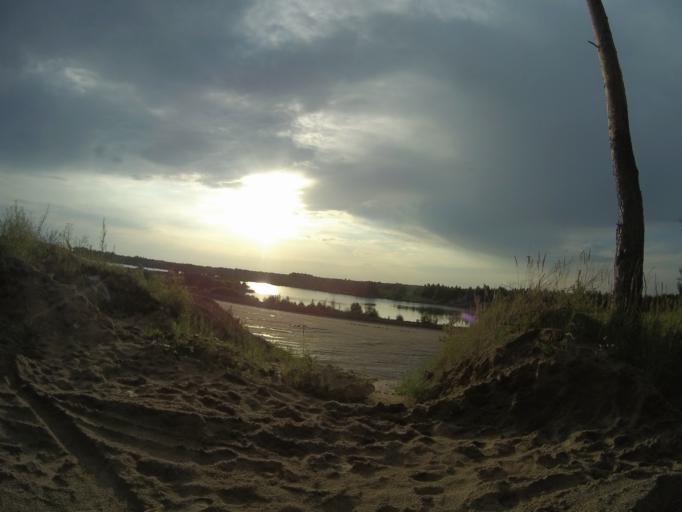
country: RU
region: Vladimir
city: Golovino
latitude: 56.0383
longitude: 40.4248
